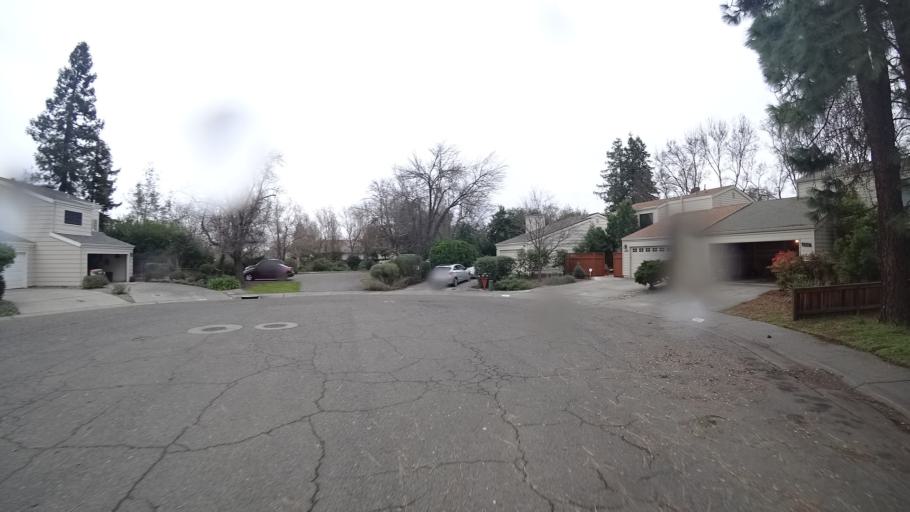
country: US
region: California
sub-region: Yolo County
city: Davis
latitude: 38.5649
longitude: -121.7263
